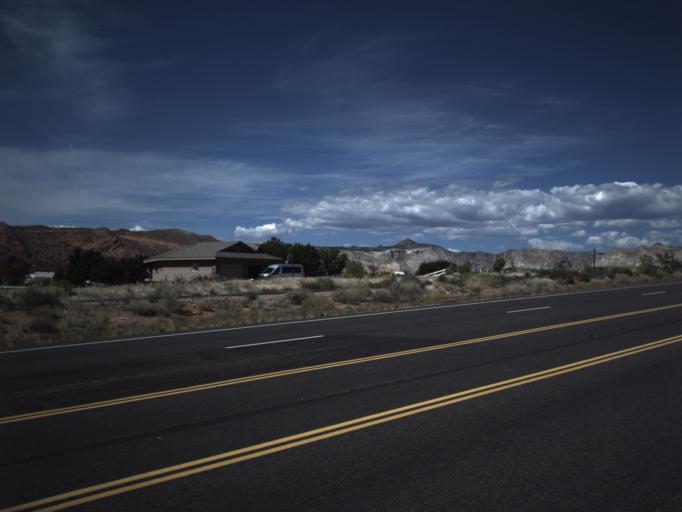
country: US
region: Utah
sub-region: Washington County
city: Santa Clara
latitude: 37.1787
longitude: -113.6189
